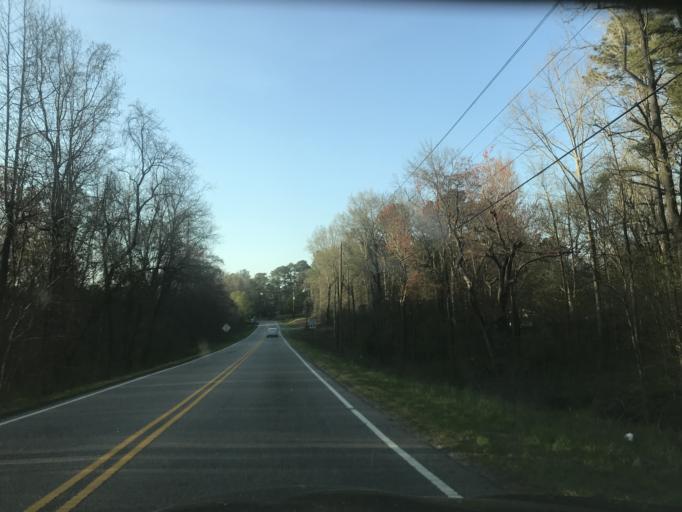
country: US
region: North Carolina
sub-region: Wake County
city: Knightdale
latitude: 35.7497
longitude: -78.5346
